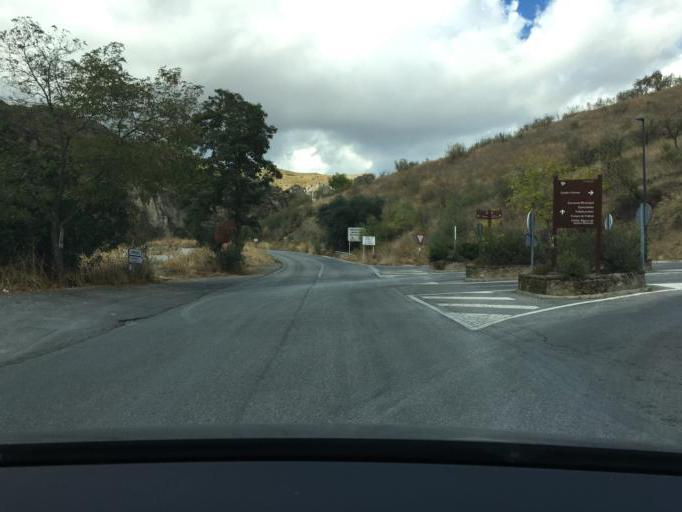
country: ES
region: Andalusia
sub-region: Provincia de Granada
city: Quentar
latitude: 37.1932
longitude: -3.4714
